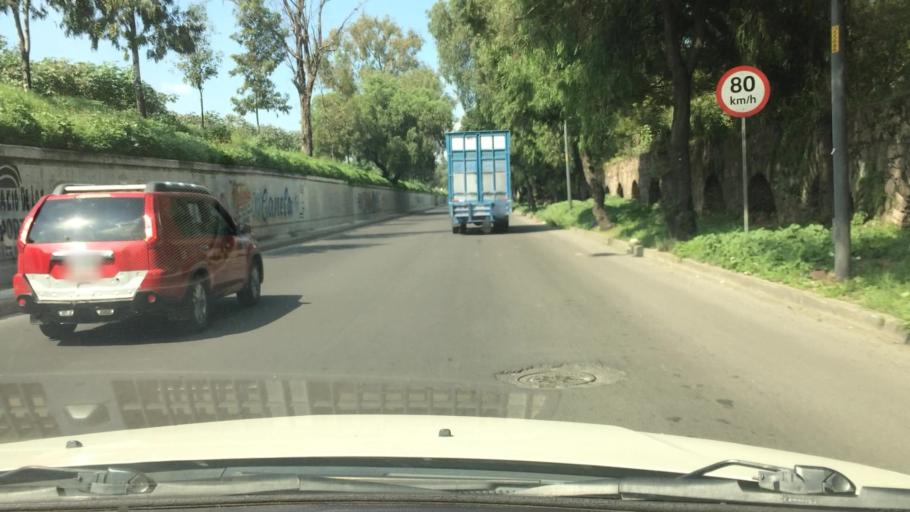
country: MX
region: Mexico
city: Colonia Lindavista
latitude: 19.5216
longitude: -99.1492
